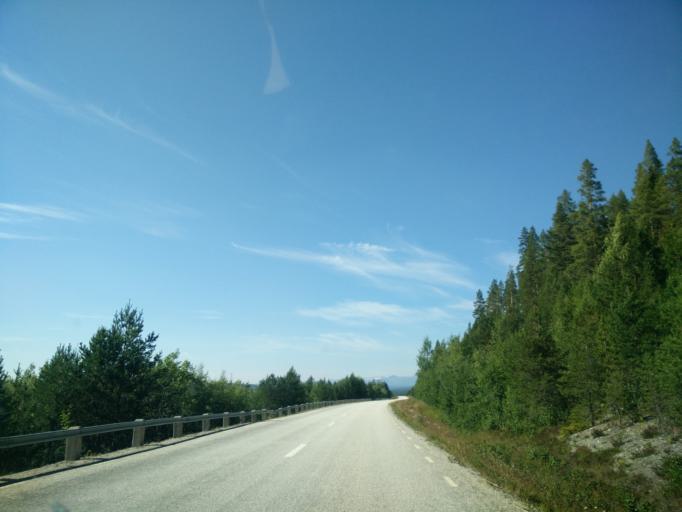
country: SE
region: Jaemtland
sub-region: Are Kommun
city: Jarpen
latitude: 62.8039
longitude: 13.5481
